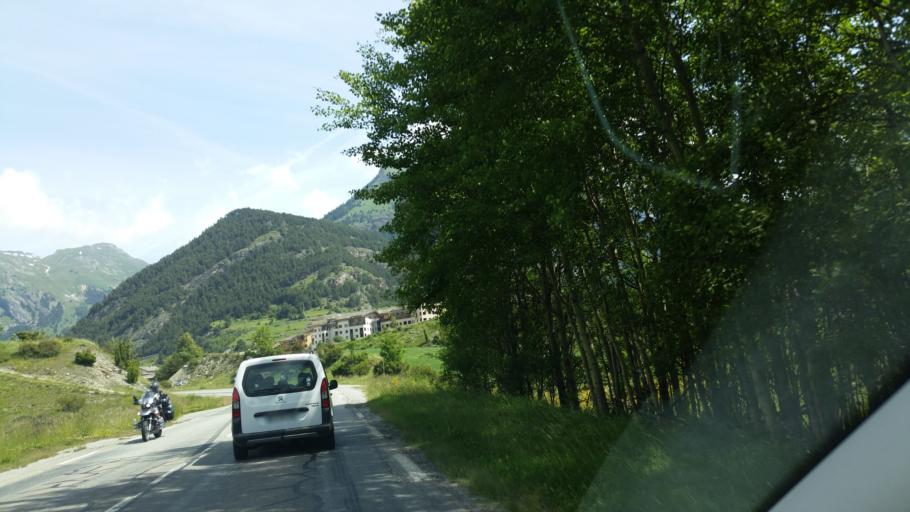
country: FR
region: Rhone-Alpes
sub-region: Departement de la Savoie
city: Modane
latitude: 45.2715
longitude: 6.8140
